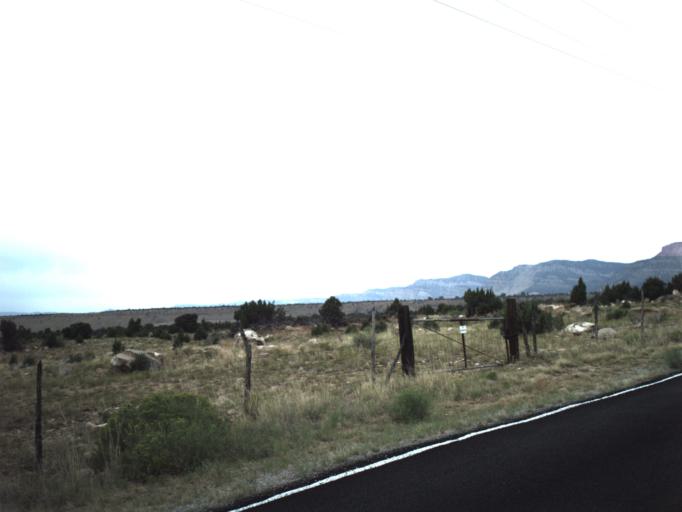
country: US
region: Utah
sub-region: Carbon County
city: East Carbon City
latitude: 39.5217
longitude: -110.3987
